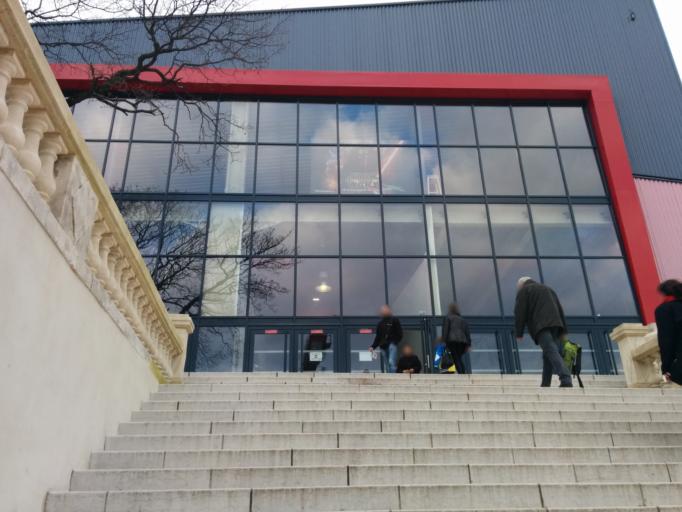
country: FR
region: Languedoc-Roussillon
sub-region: Departement du Gard
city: Ales
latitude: 44.1264
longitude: 4.0781
